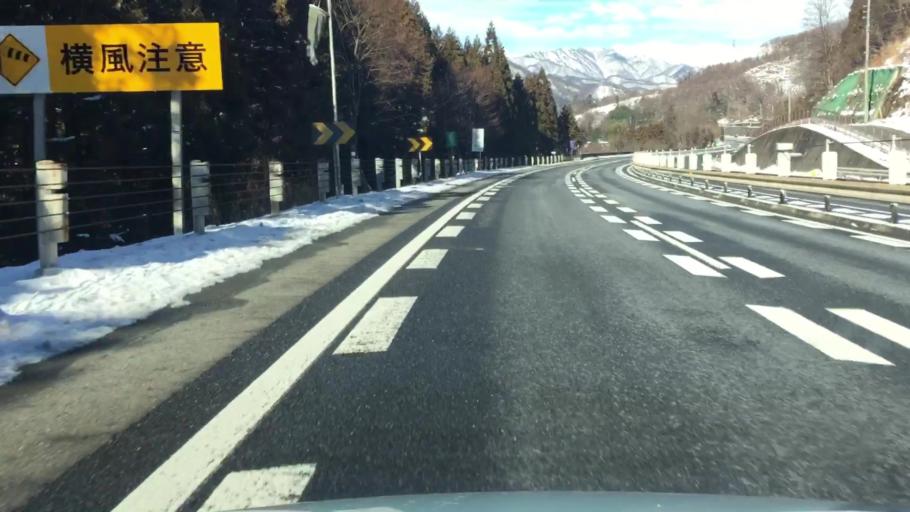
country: JP
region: Gunma
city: Numata
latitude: 36.6927
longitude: 138.9939
